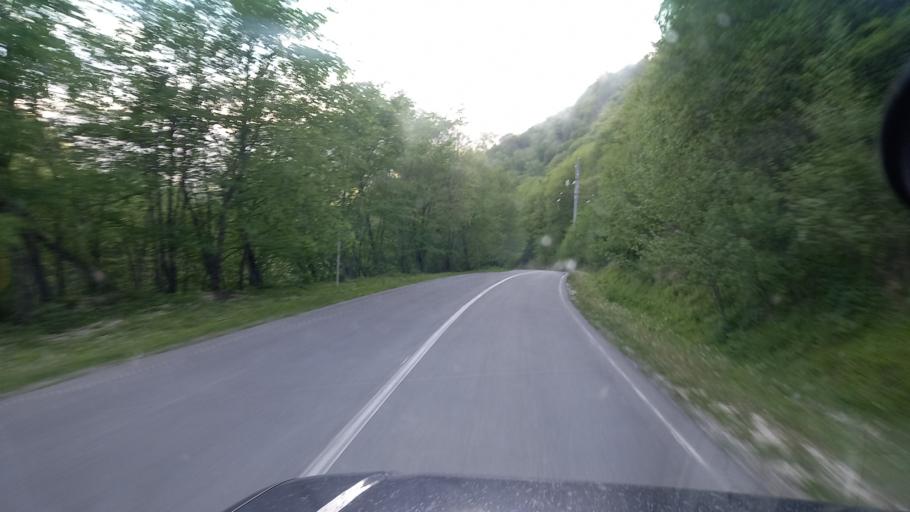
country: RU
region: North Ossetia
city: Tarskoye
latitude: 42.9025
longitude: 44.9525
